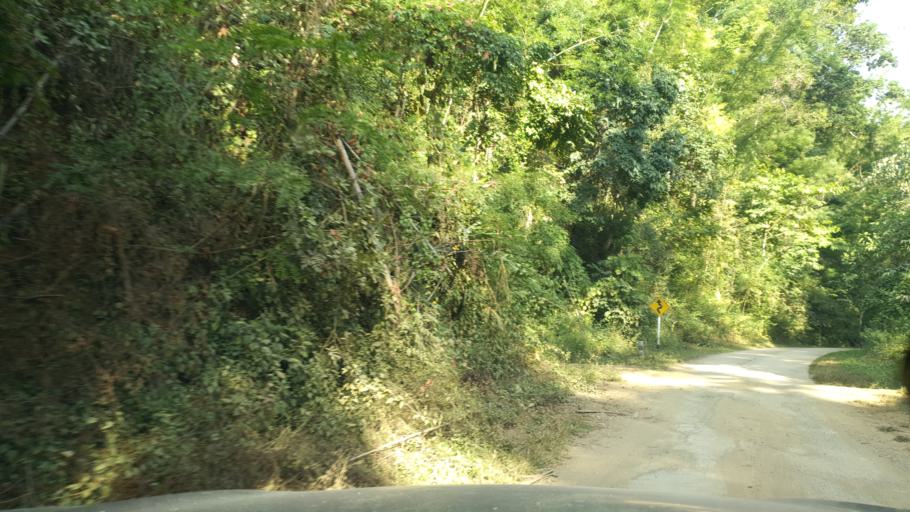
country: TH
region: Chiang Mai
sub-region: Amphoe Chiang Dao
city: Chiang Dao
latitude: 19.4110
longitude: 98.7898
